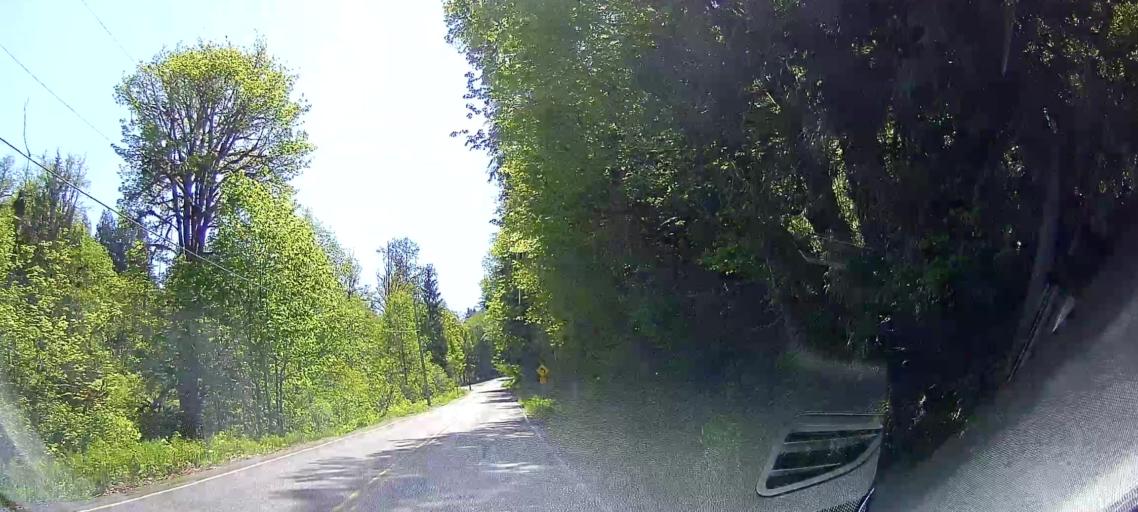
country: US
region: Washington
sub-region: Snohomish County
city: Darrington
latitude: 48.4741
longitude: -121.6440
